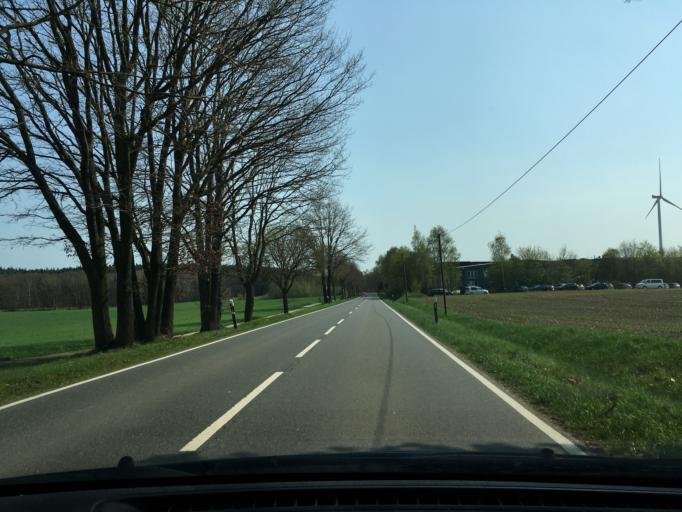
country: DE
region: Lower Saxony
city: Sudergellersen
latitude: 53.2014
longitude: 10.3024
